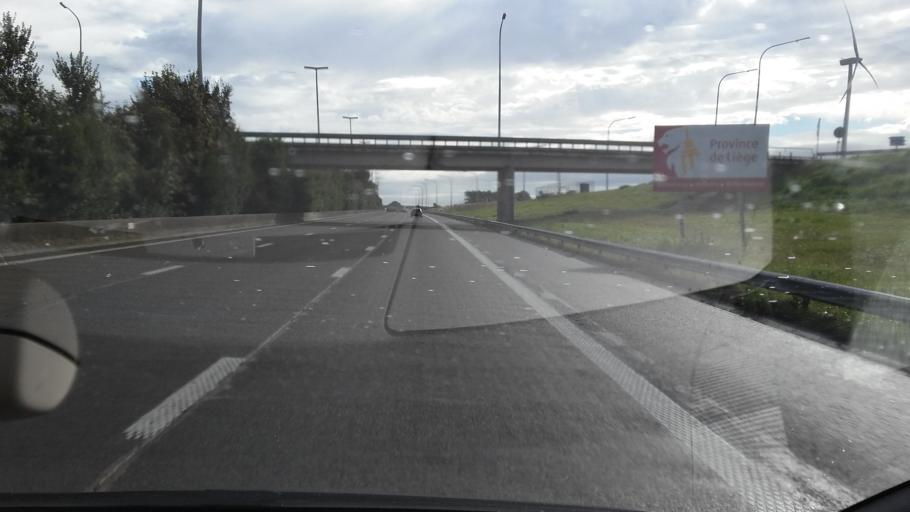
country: BE
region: Wallonia
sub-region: Province de Liege
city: Berloz
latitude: 50.7001
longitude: 5.1849
